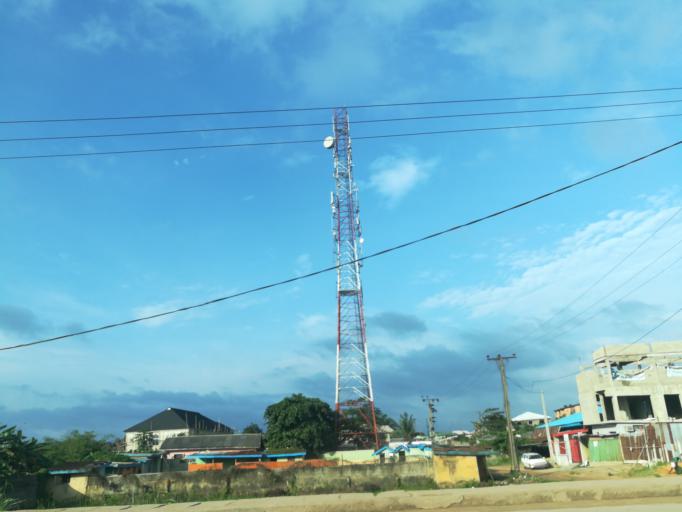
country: NG
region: Lagos
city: Ebute Ikorodu
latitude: 6.6112
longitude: 3.4831
